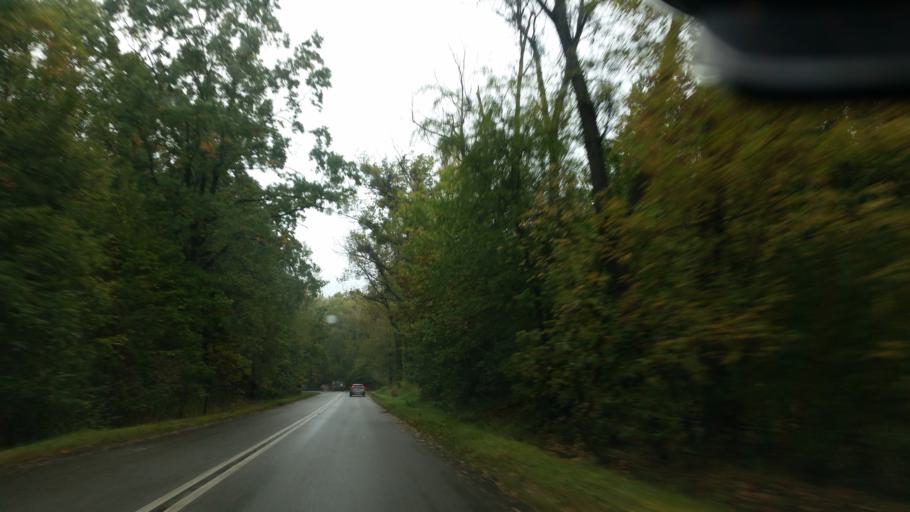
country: PL
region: Masovian Voivodeship
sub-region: Powiat warszawski zachodni
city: Babice
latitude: 52.2719
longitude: 20.8746
